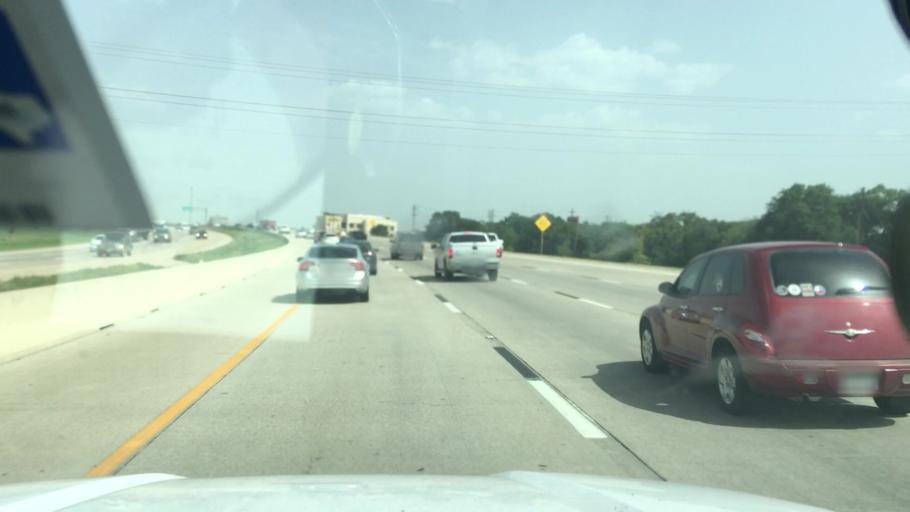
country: US
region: Texas
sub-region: Tarrant County
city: Southlake
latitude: 32.9633
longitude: -97.1552
